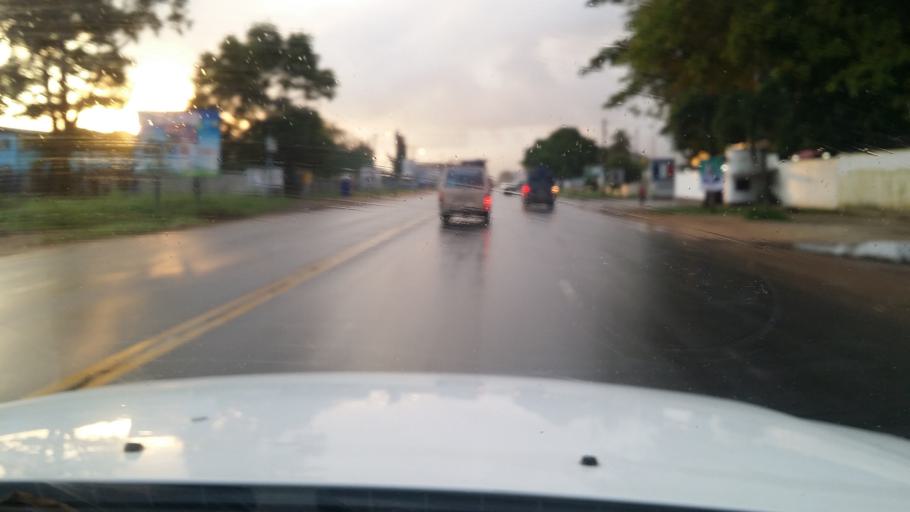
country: LR
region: Montserrado
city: Monrovia
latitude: 6.2783
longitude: -10.7597
